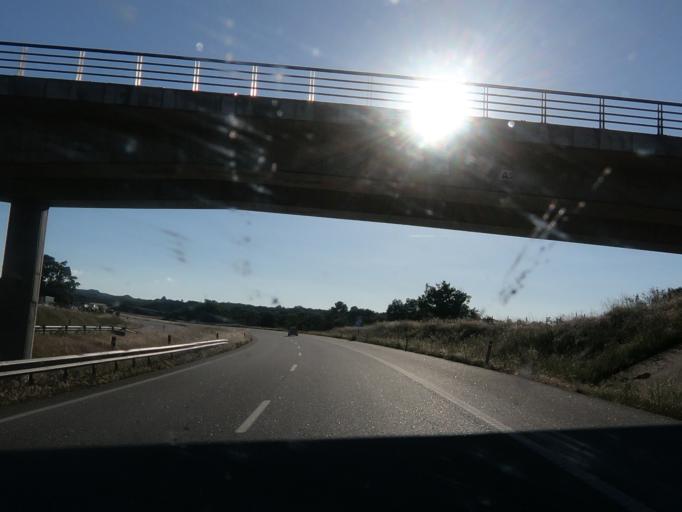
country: PT
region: Guarda
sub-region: Guarda
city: Sequeira
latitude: 40.6027
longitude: -7.1021
